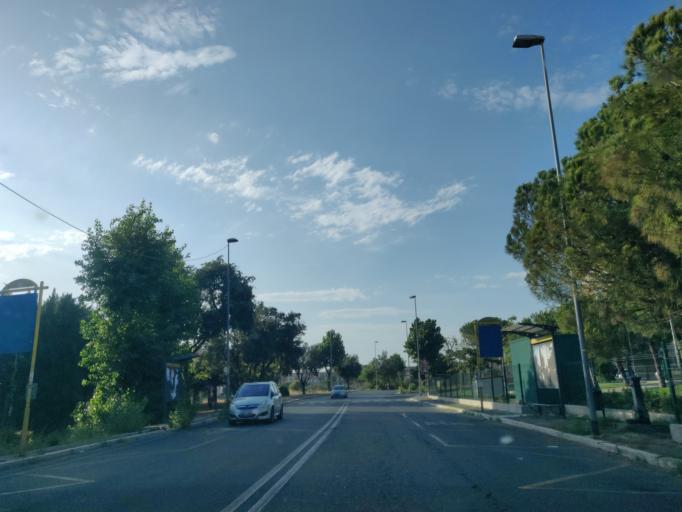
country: IT
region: Latium
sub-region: Citta metropolitana di Roma Capitale
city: Civitavecchia
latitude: 42.0782
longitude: 11.8146
